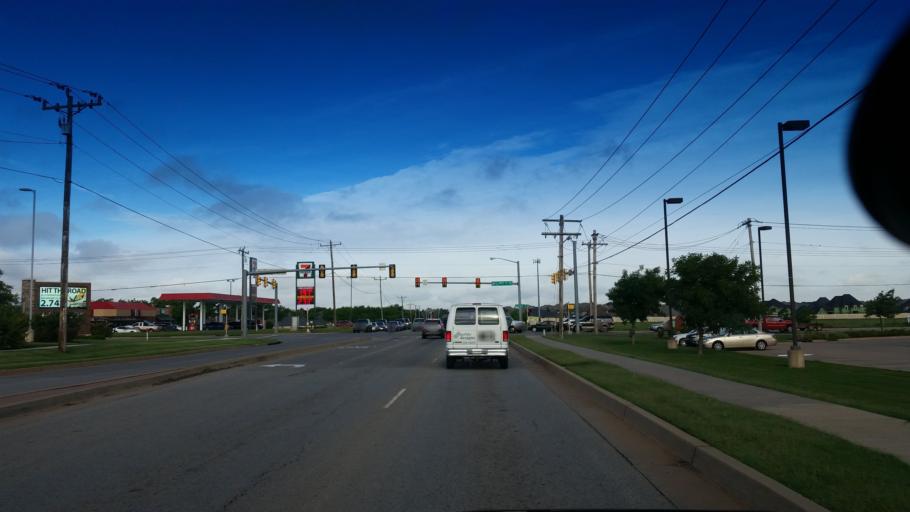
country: US
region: Oklahoma
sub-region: Oklahoma County
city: Edmond
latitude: 35.6238
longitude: -97.5128
